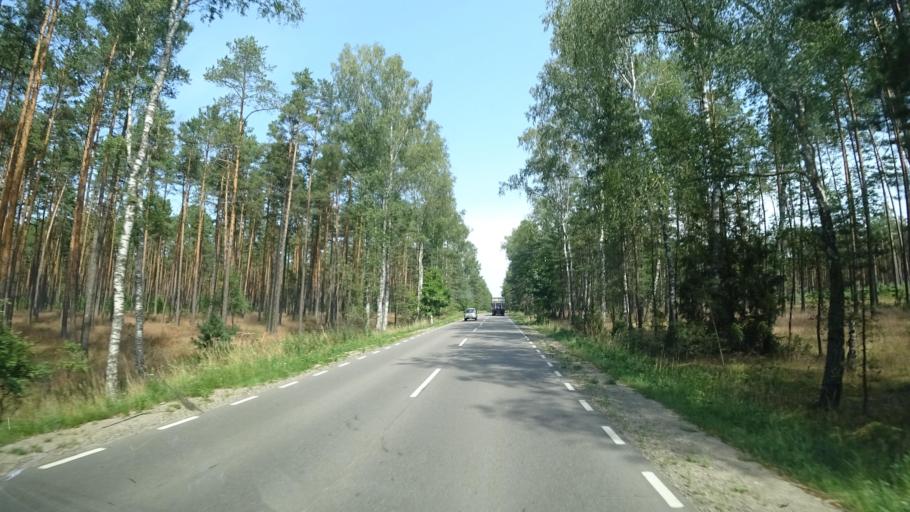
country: PL
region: Pomeranian Voivodeship
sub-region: Powiat koscierski
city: Lipusz
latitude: 54.1013
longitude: 17.8183
